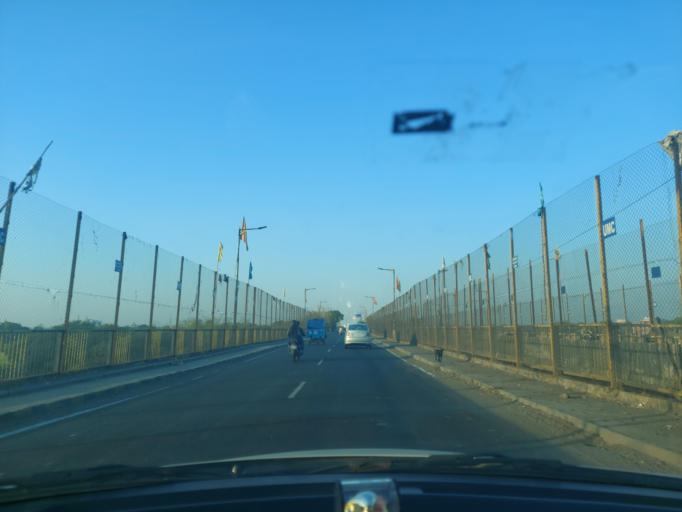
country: IN
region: Madhya Pradesh
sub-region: Ujjain
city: Ujjain
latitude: 23.1291
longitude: 75.7956
